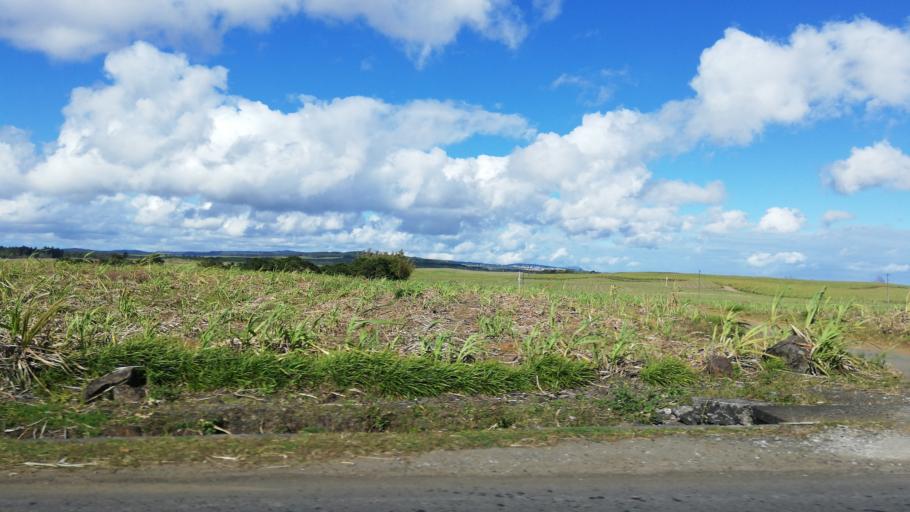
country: MU
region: Moka
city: Quartier Militaire
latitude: -20.2413
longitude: 57.5835
